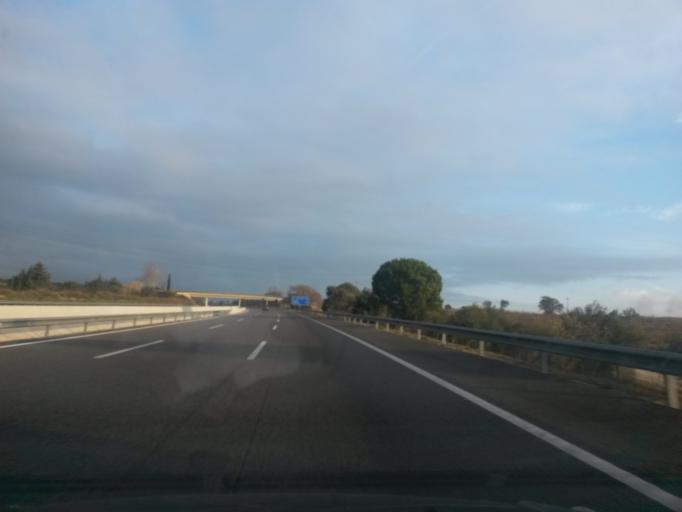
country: ES
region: Catalonia
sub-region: Provincia de Girona
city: Vilafant
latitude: 42.2523
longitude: 2.9438
